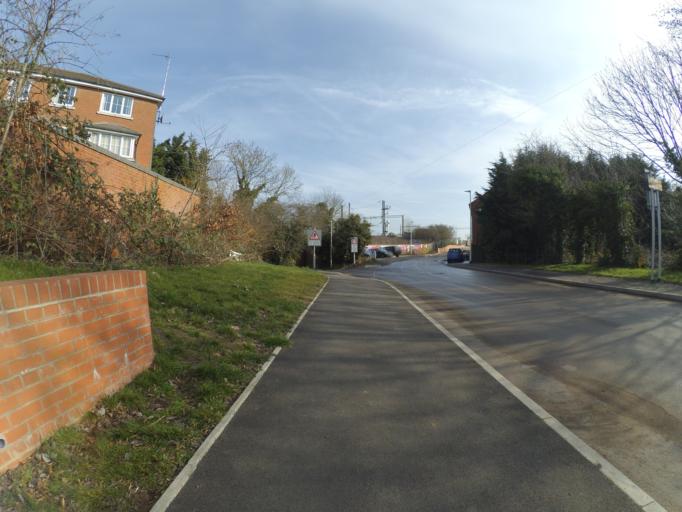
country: GB
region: England
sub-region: Warwickshire
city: Rugby
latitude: 52.3605
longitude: -1.2078
